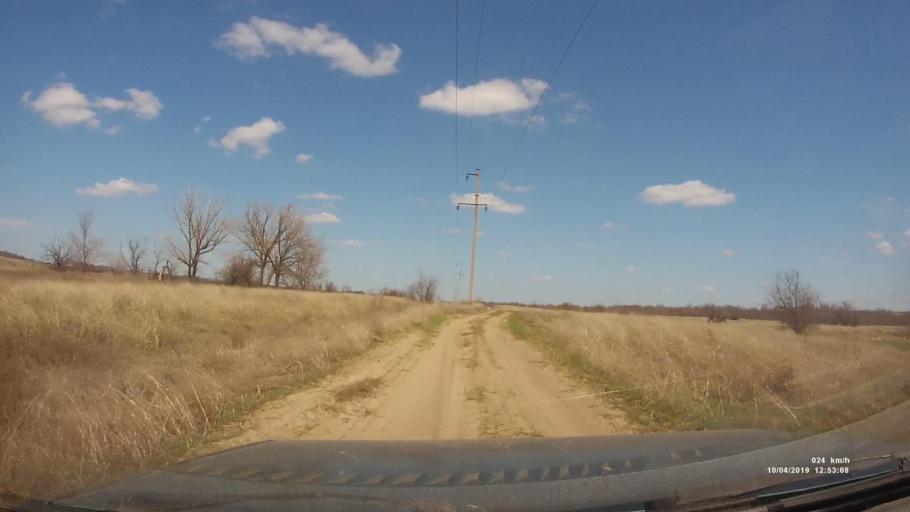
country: RU
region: Rostov
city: Masalovka
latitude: 48.3632
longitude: 40.2200
